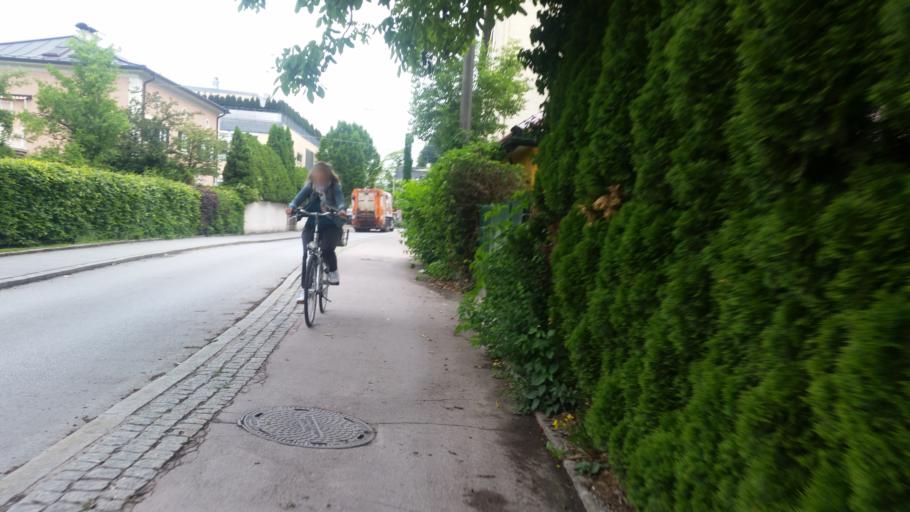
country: AT
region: Salzburg
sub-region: Salzburg Stadt
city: Salzburg
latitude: 47.7992
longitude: 13.0324
